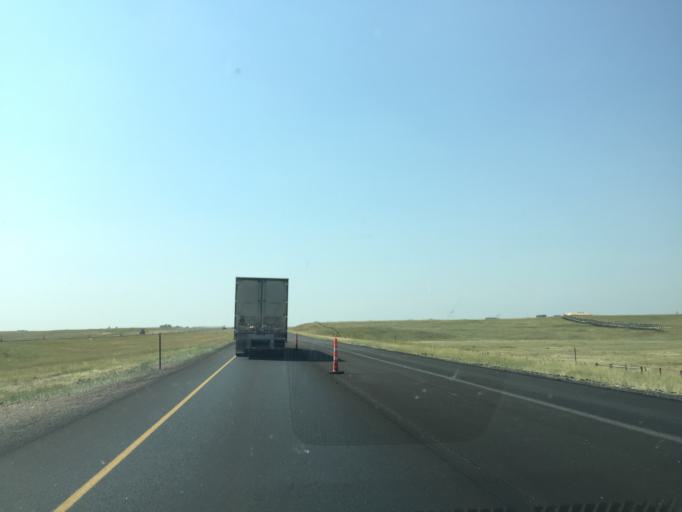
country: US
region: Wyoming
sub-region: Laramie County
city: Ranchettes
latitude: 41.3095
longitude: -104.8573
